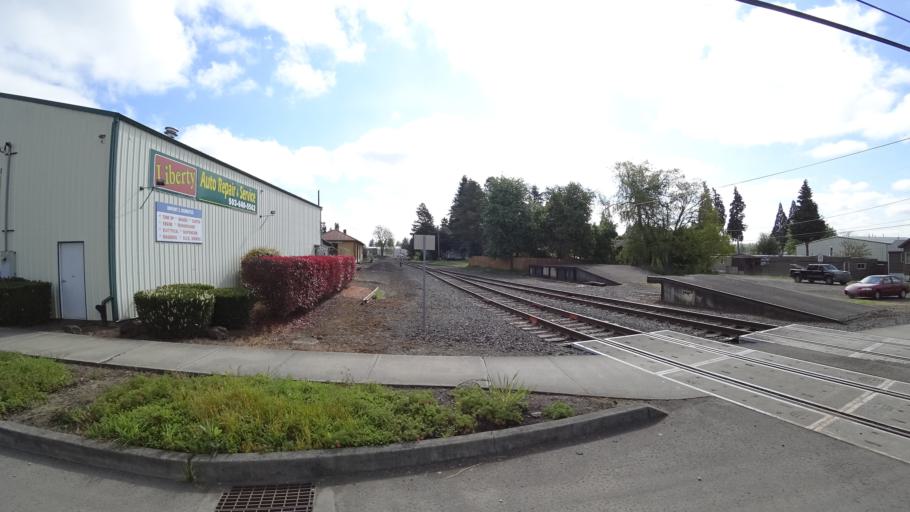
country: US
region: Oregon
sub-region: Washington County
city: Hillsboro
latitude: 45.5160
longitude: -122.9899
